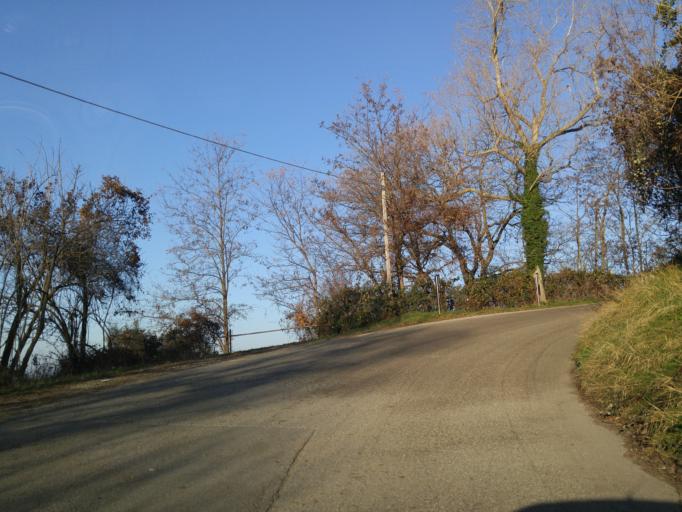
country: IT
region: The Marches
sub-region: Provincia di Pesaro e Urbino
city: Mombaroccio
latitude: 43.7847
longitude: 12.8501
